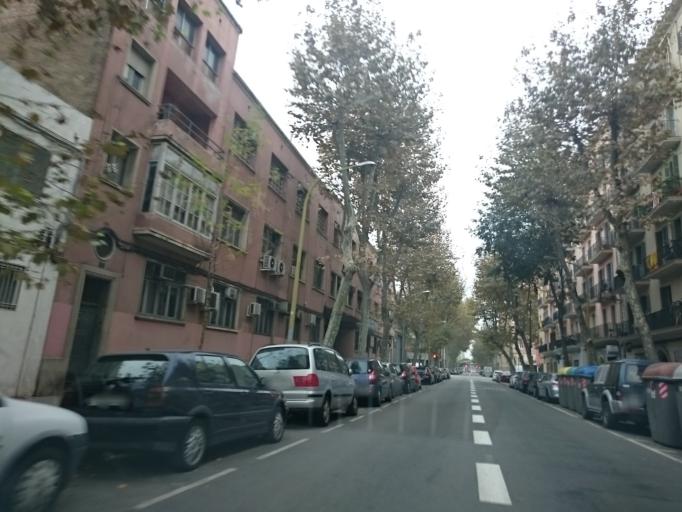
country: ES
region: Catalonia
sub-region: Provincia de Barcelona
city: Sant Marti
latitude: 41.4099
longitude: 2.1986
